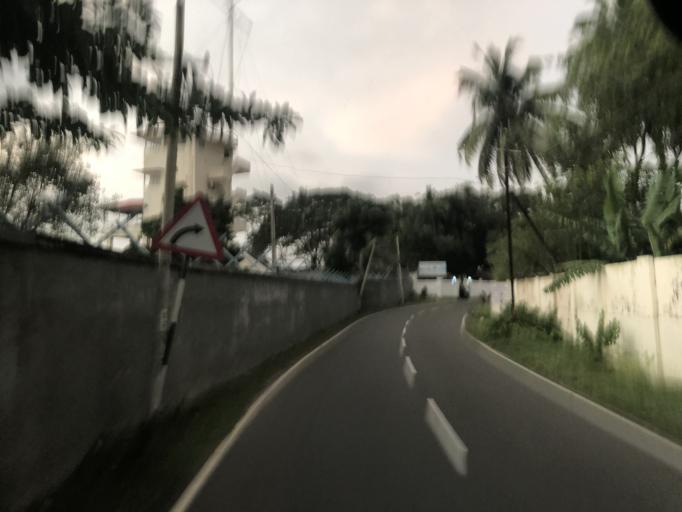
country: IN
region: Kerala
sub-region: Ernakulam
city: Cochin
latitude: 9.9618
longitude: 76.2377
